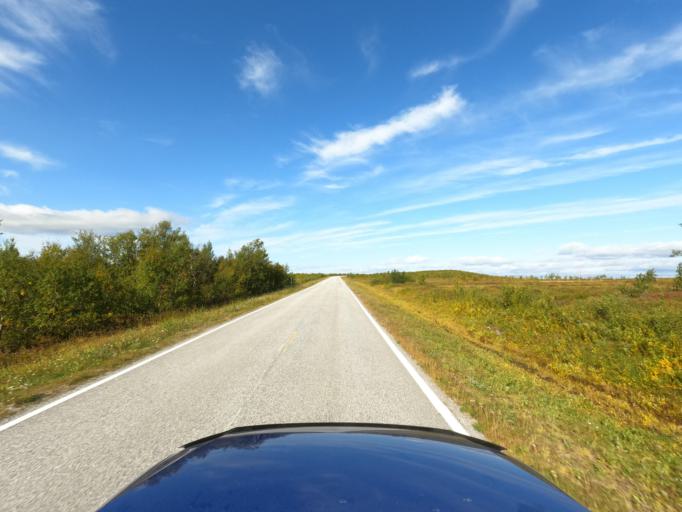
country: NO
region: Finnmark Fylke
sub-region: Karasjok
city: Karasjohka
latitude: 69.7080
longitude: 25.2456
